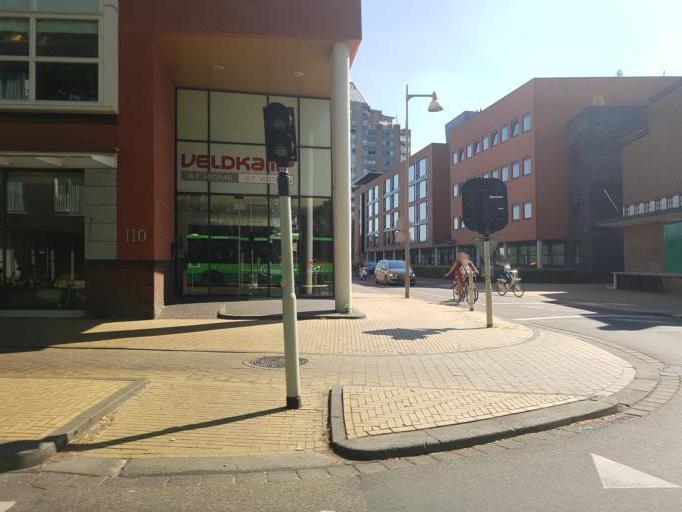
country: NL
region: Gelderland
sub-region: Gemeente Apeldoorn
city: Apeldoorn
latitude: 52.2136
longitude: 5.9669
